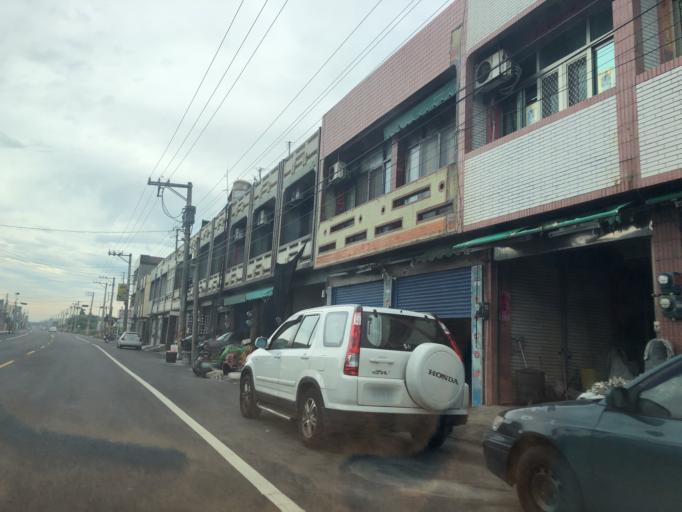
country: TW
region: Taiwan
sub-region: Chiayi
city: Taibao
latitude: 23.7041
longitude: 120.2003
